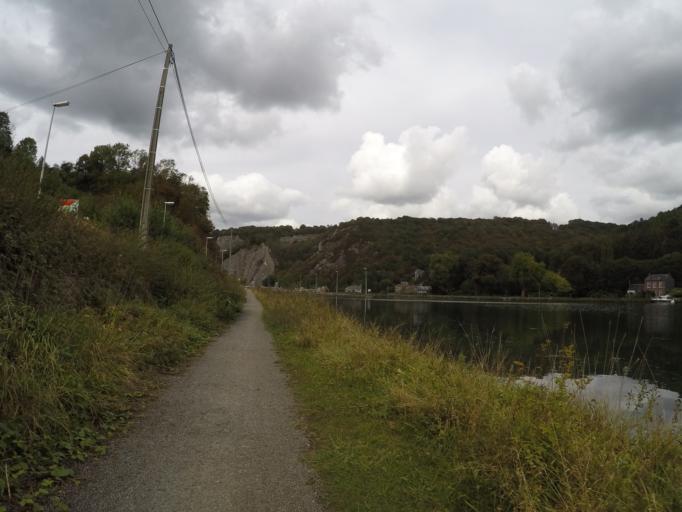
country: BE
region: Wallonia
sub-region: Province de Namur
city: Yvoir
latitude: 50.3324
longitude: 4.8717
